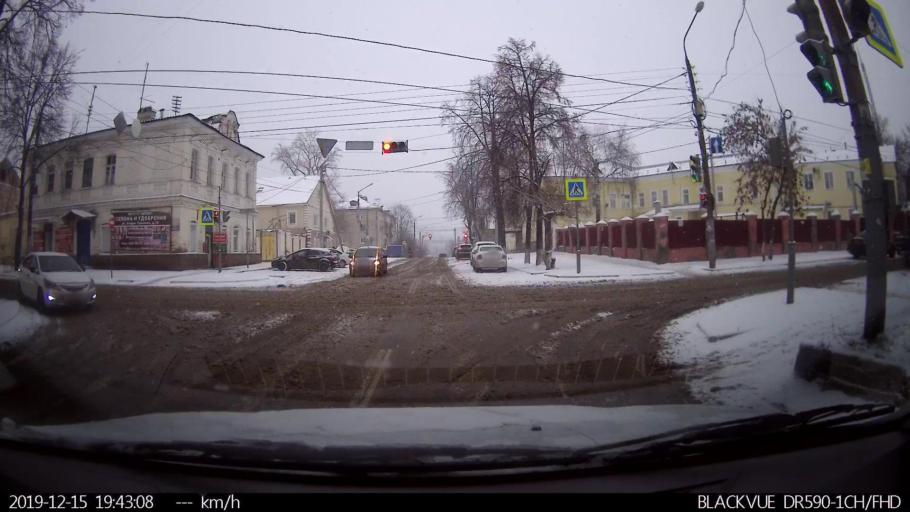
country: RU
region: Nizjnij Novgorod
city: Sarov
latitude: 54.9601
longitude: 43.5440
